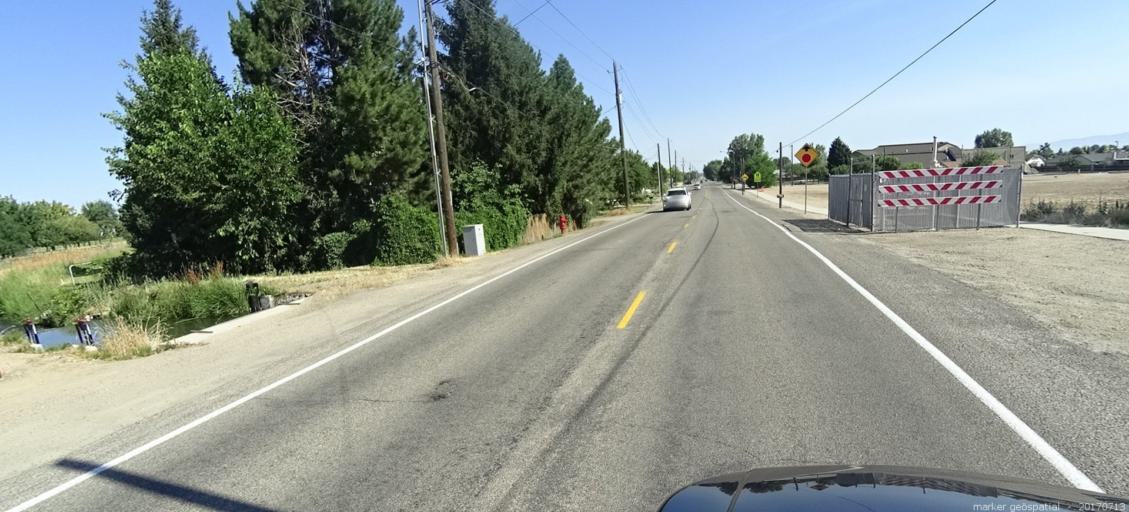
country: US
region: Idaho
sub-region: Ada County
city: Kuna
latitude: 43.4944
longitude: -116.4136
